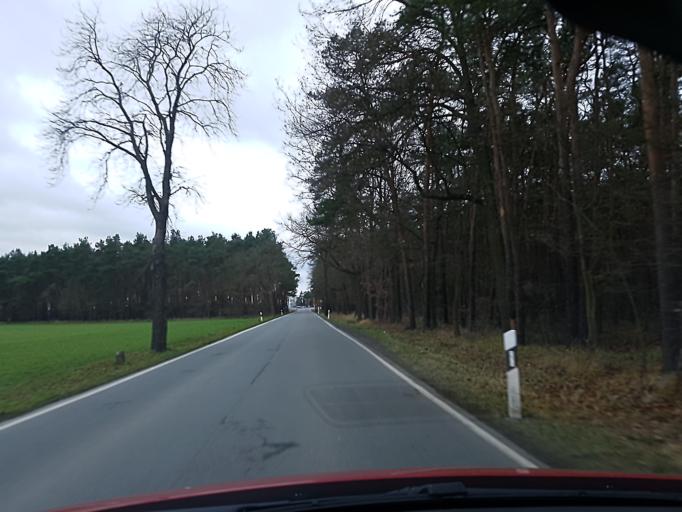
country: DE
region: Brandenburg
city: Bad Liebenwerda
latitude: 51.5340
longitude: 13.4032
